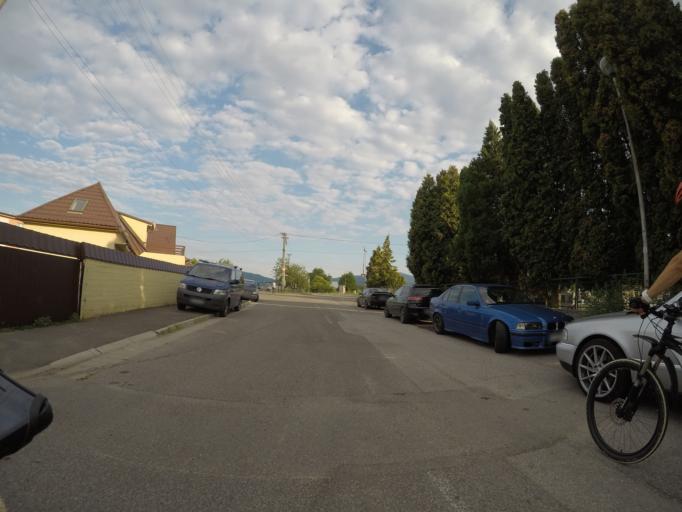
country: SK
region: Trenciansky
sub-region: Okres Trencin
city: Trencin
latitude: 48.8921
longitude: 17.9990
